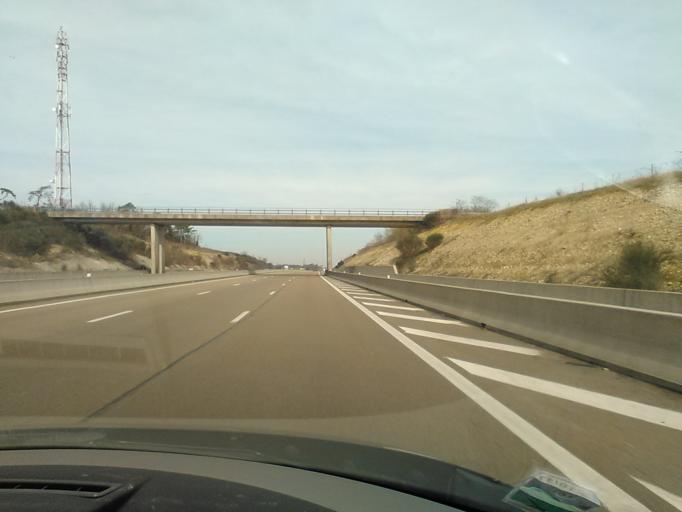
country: FR
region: Bourgogne
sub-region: Departement de la Cote-d'Or
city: Saint-Julien
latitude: 47.4505
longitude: 5.1711
